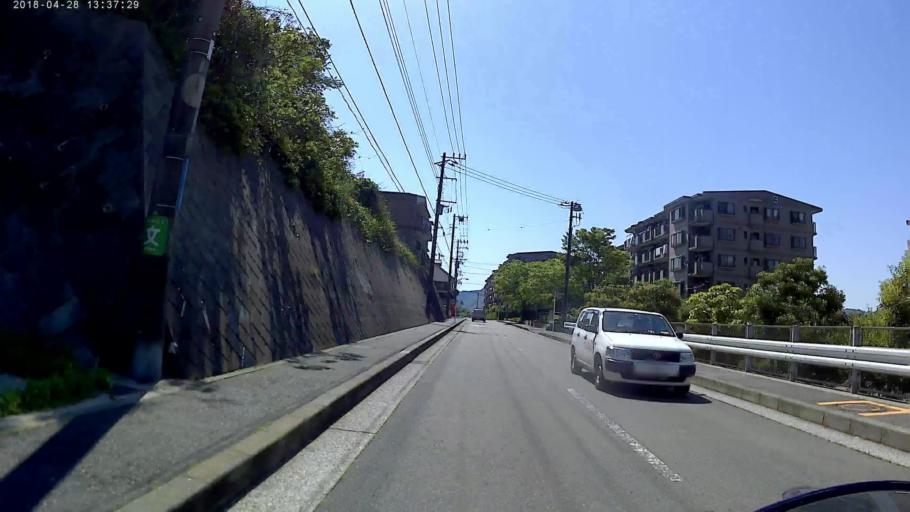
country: JP
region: Kanagawa
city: Yokosuka
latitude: 35.2167
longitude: 139.6915
